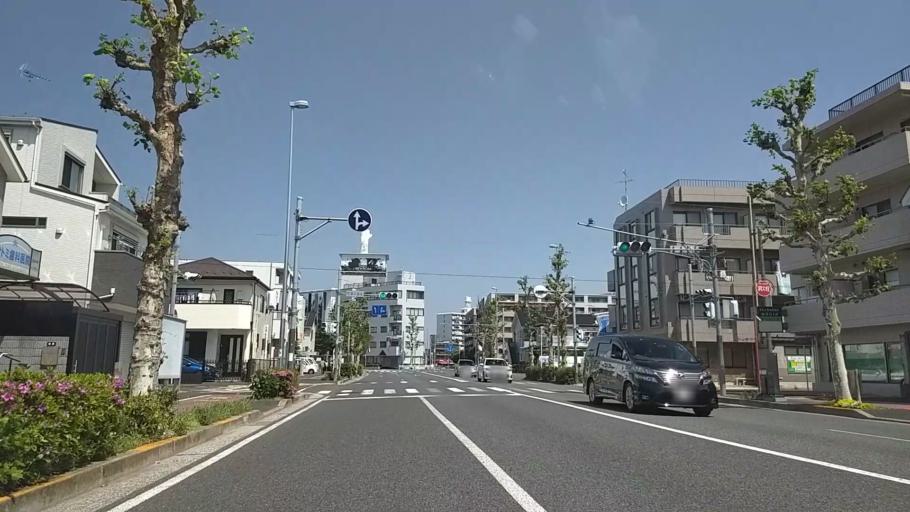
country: JP
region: Kanagawa
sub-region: Kawasaki-shi
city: Kawasaki
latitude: 35.5161
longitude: 139.6900
